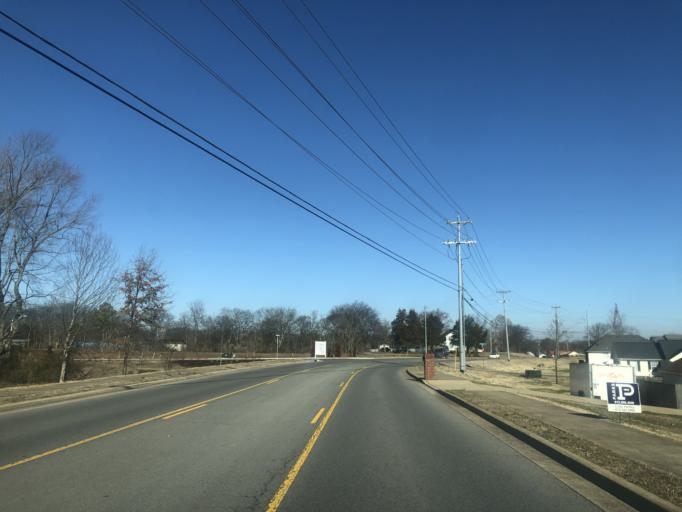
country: US
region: Tennessee
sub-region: Rutherford County
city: Smyrna
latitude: 35.8963
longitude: -86.4781
